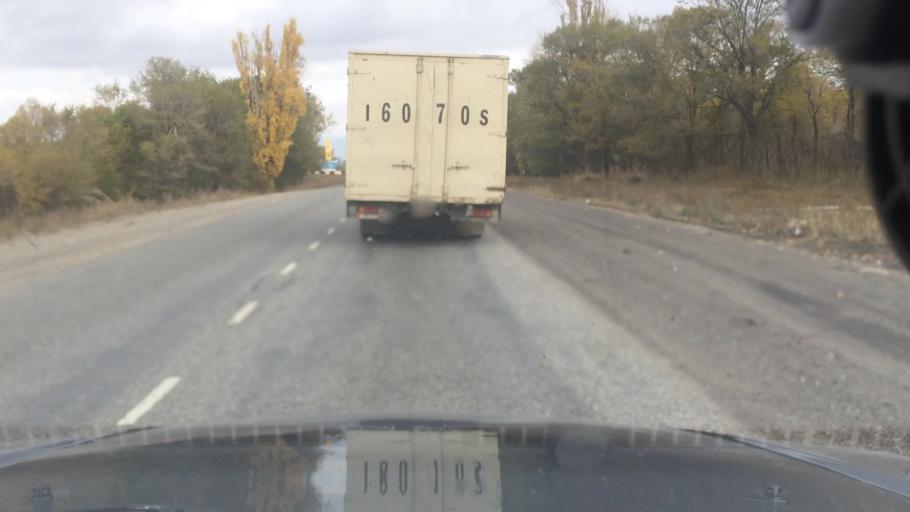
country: KG
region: Ysyk-Koel
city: Tyup
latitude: 42.6647
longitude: 78.3497
